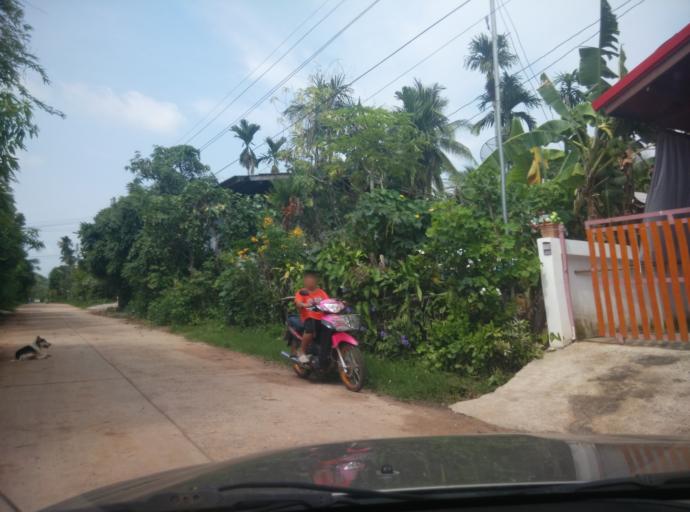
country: TH
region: Sisaket
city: Huai Thap Than
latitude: 15.0283
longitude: 104.0722
